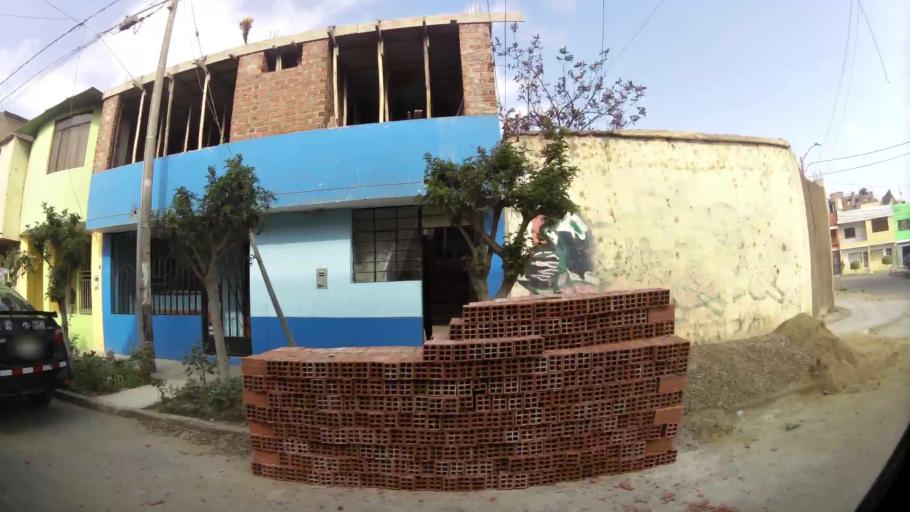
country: PE
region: La Libertad
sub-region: Provincia de Trujillo
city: Trujillo
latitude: -8.1068
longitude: -79.0136
